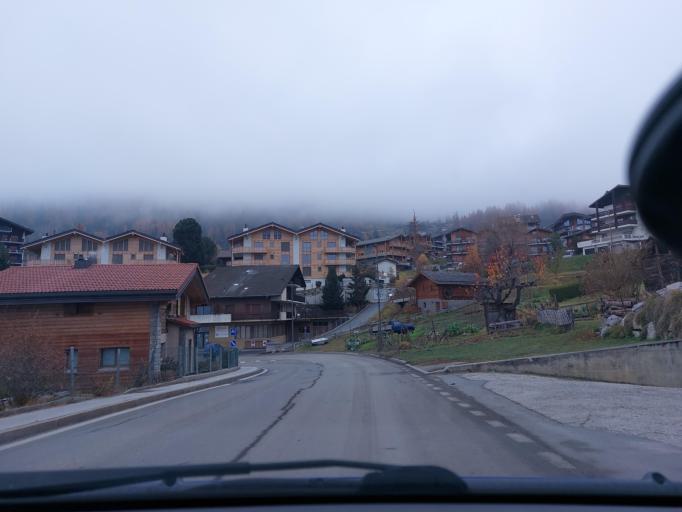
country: CH
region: Valais
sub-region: Conthey District
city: Basse-Nendaz
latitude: 46.1845
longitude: 7.2959
